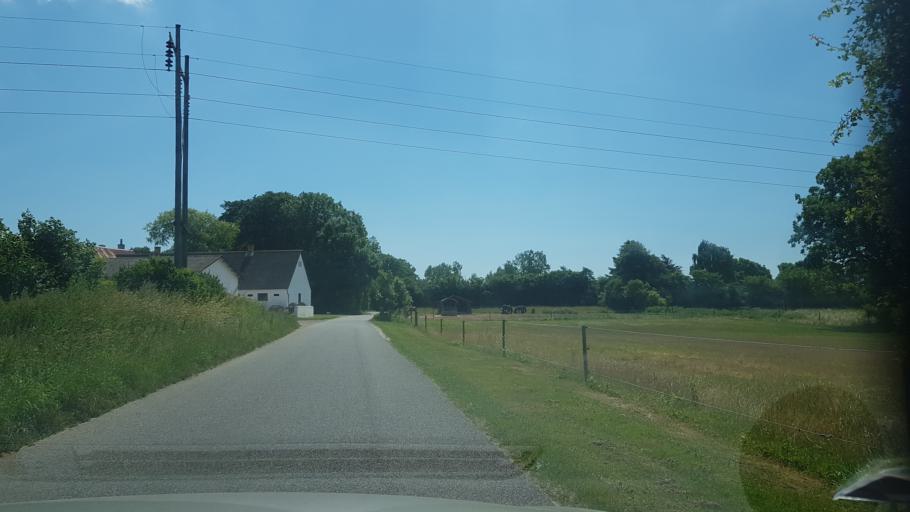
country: DK
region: Zealand
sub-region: Kalundborg Kommune
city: Svebolle
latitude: 55.7011
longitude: 11.2927
